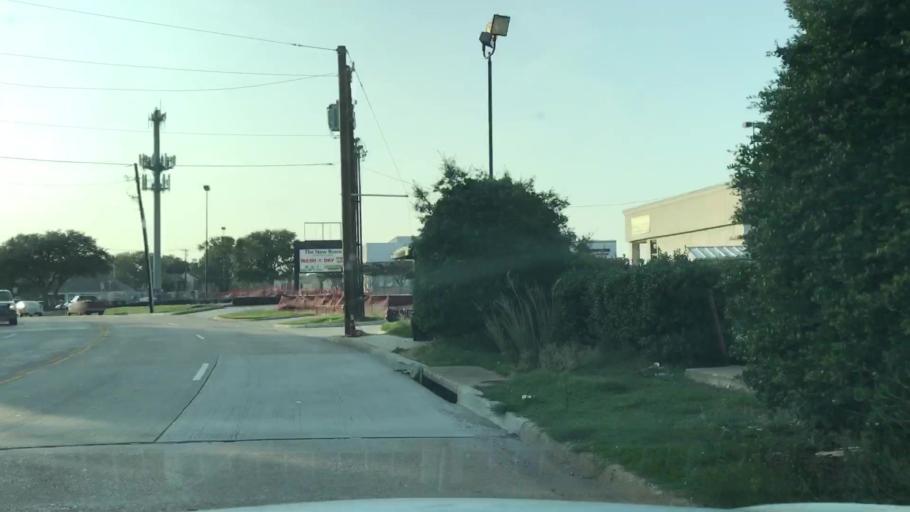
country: US
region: Texas
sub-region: Dallas County
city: Richardson
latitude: 32.8992
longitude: -96.7196
